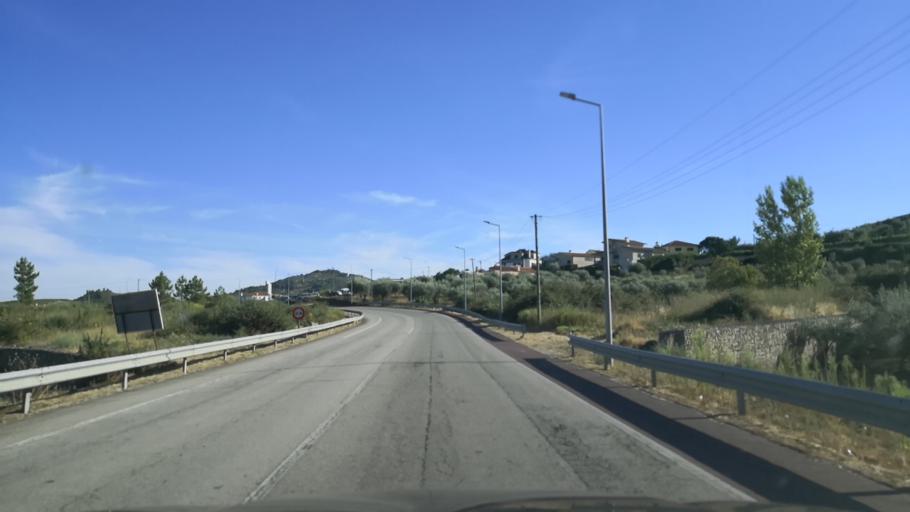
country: PT
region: Vila Real
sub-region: Murca
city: Murca
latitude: 41.4009
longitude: -7.4468
